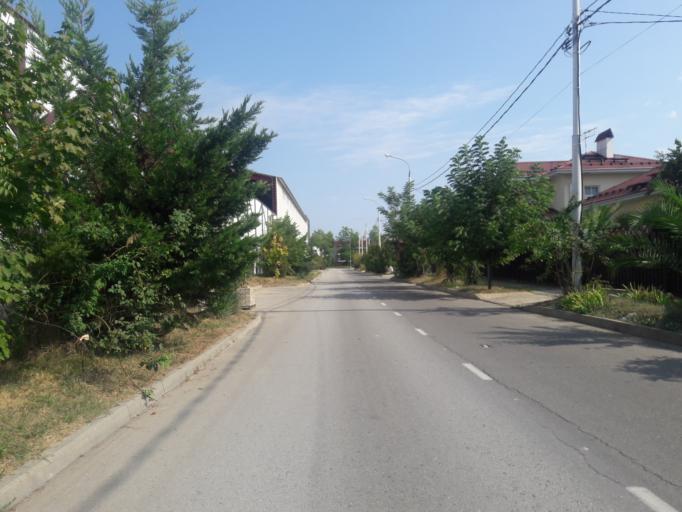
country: RU
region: Krasnodarskiy
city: Vysokoye
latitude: 43.3952
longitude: 40.0011
